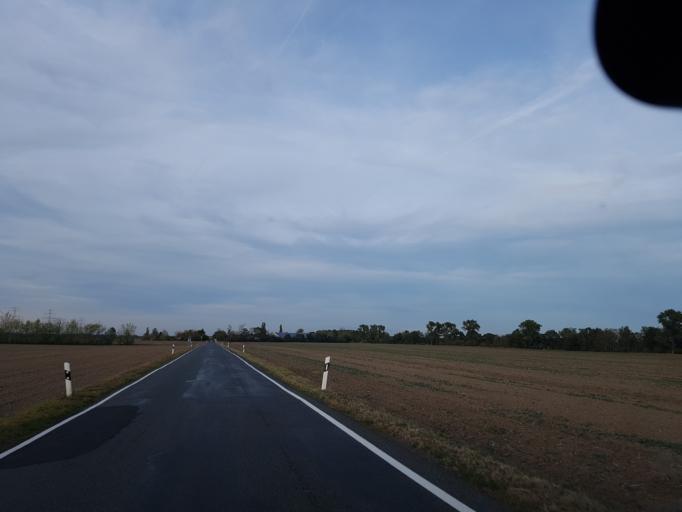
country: DE
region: Saxony
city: Wulknitz
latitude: 51.3481
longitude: 13.3948
